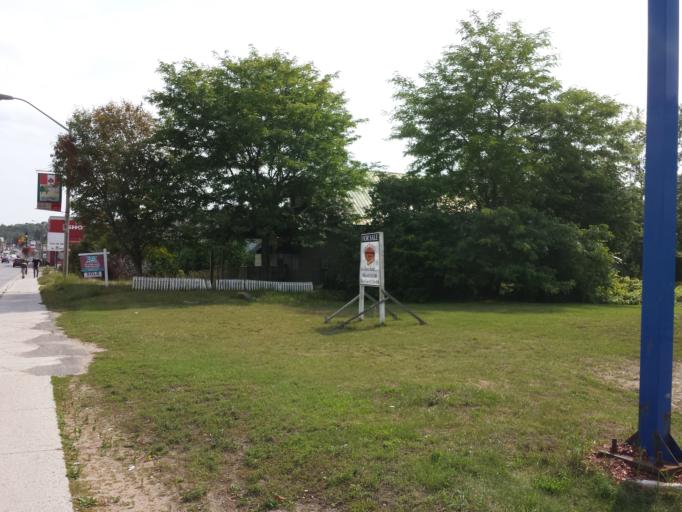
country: CA
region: Ontario
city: Bancroft
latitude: 45.0629
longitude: -77.8571
